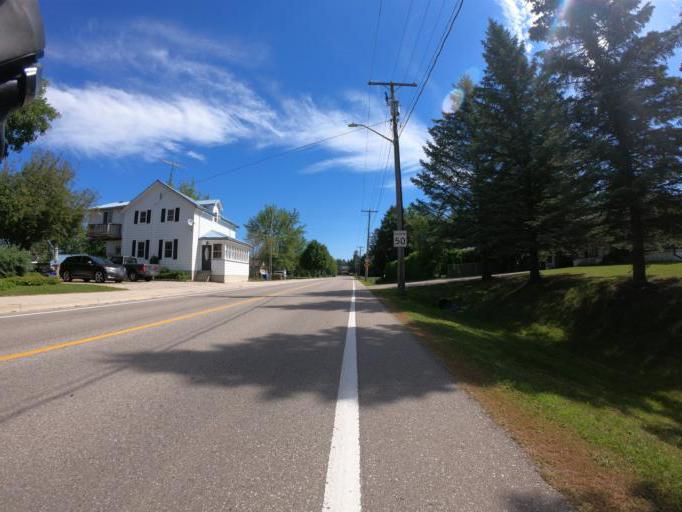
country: CA
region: Ontario
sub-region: Wellington County
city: Guelph
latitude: 43.5353
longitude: -80.3881
